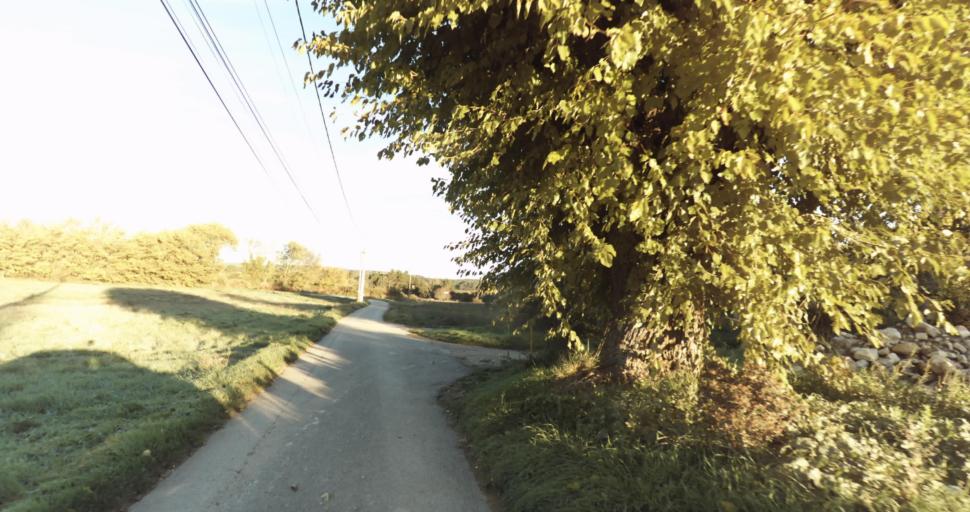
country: FR
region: Provence-Alpes-Cote d'Azur
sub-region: Departement des Bouches-du-Rhone
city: Venelles
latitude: 43.5779
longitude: 5.5005
